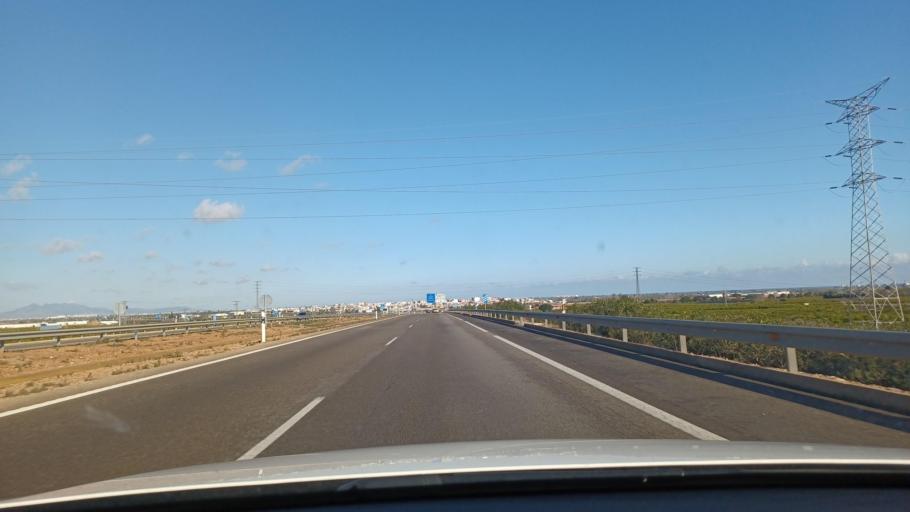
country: ES
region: Valencia
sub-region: Provincia de Castello
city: Villavieja
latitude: 39.8399
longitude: -0.1868
